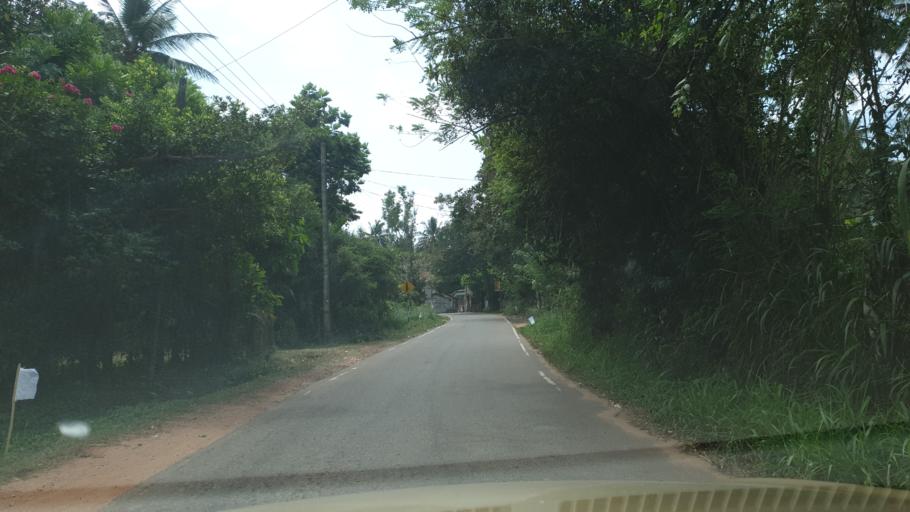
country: LK
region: North Western
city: Kuliyapitiya
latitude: 7.3635
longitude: 79.9669
